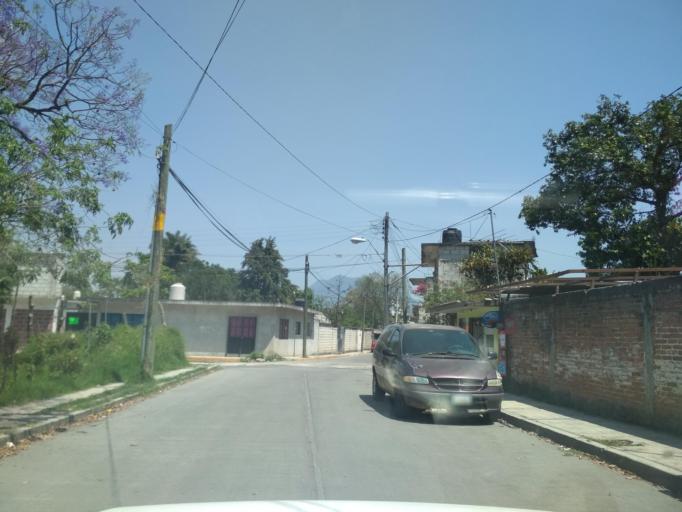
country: MX
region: Veracruz
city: Rio Blanco
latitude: 18.8343
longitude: -97.1126
